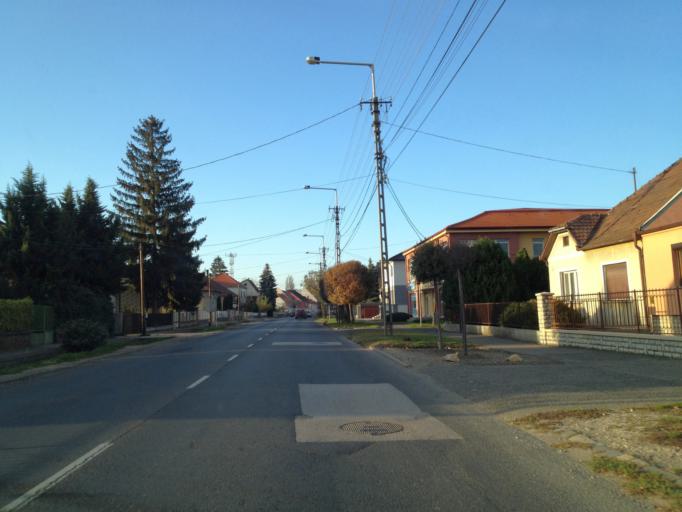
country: HU
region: Gyor-Moson-Sopron
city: Gyor
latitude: 47.6606
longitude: 17.6529
